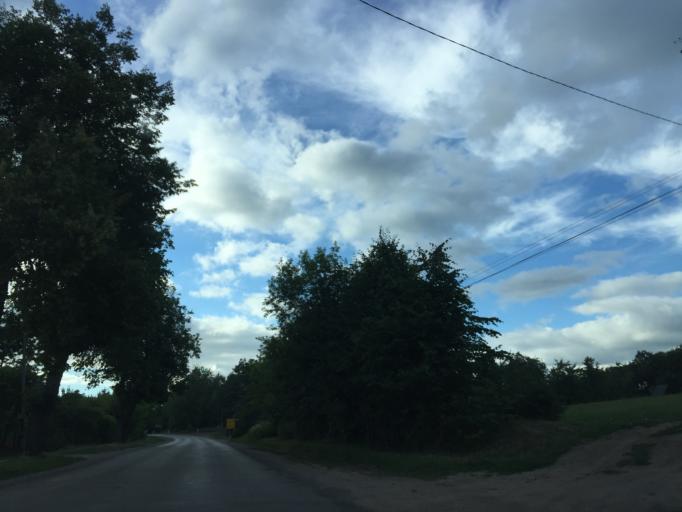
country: LV
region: Rezekne
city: Rezekne
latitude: 56.5299
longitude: 27.3158
